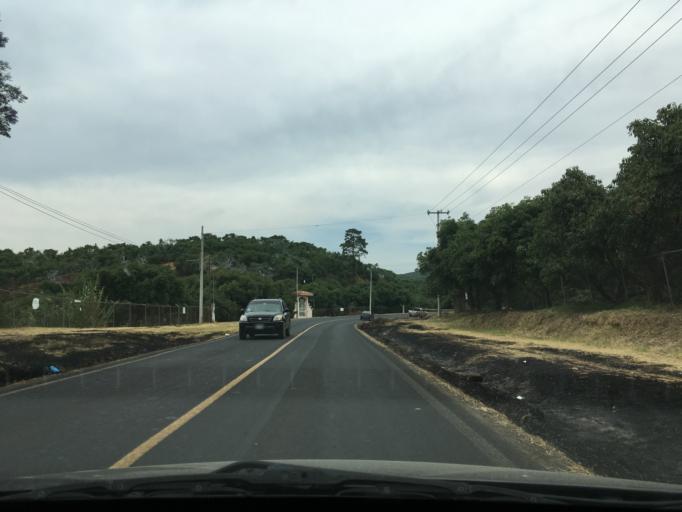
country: MX
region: Michoacan
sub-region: Uruapan
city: Uruapan
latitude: 19.3863
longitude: -102.0957
